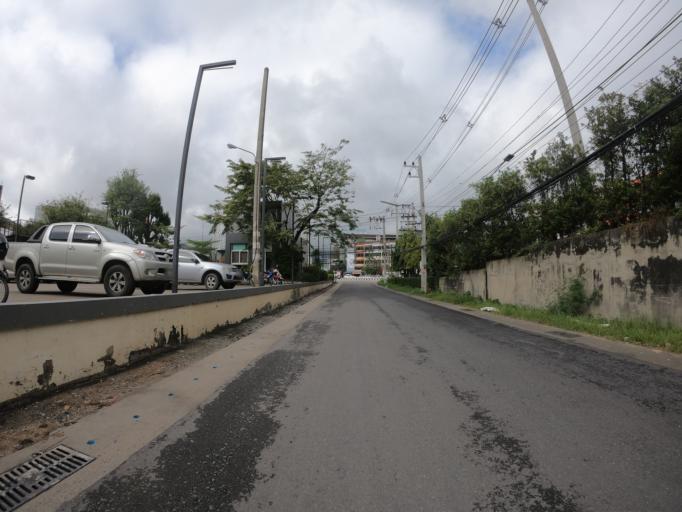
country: TH
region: Chiang Mai
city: Chiang Mai
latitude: 18.8046
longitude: 98.9704
